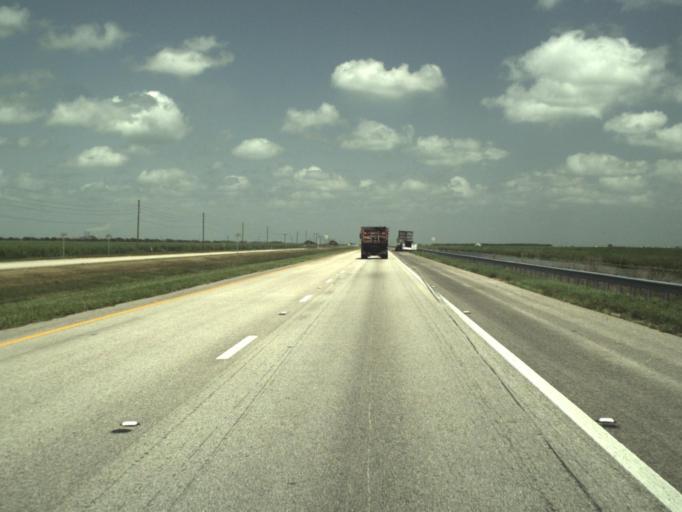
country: US
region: Florida
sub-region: Palm Beach County
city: Belle Glade Camp
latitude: 26.5426
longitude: -80.6986
